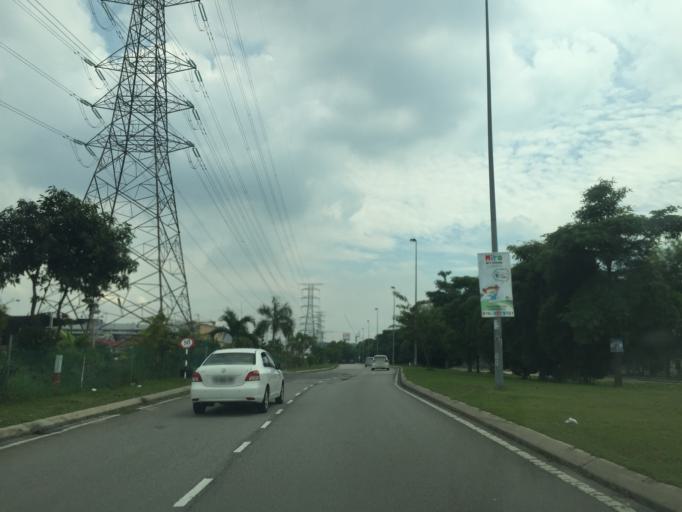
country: MY
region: Selangor
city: Klang
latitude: 2.9913
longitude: 101.4387
